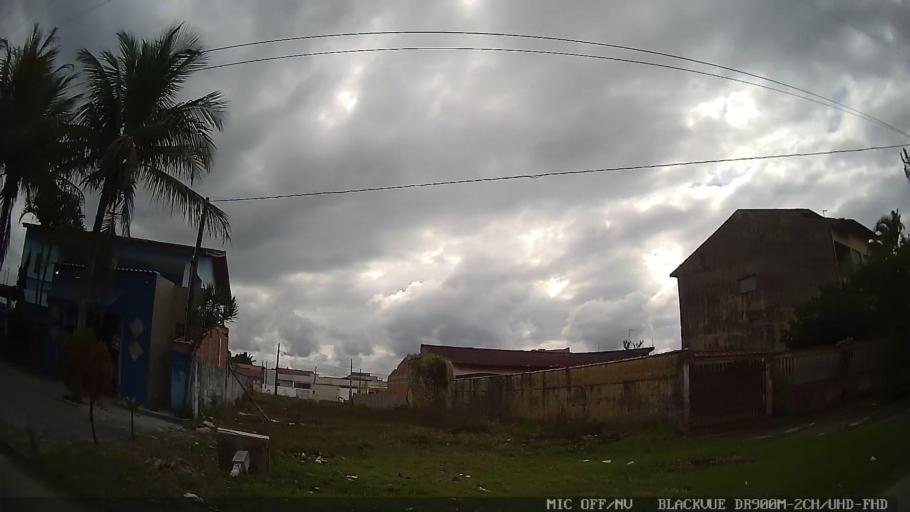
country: BR
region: Sao Paulo
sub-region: Itanhaem
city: Itanhaem
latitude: -24.2352
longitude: -46.8821
